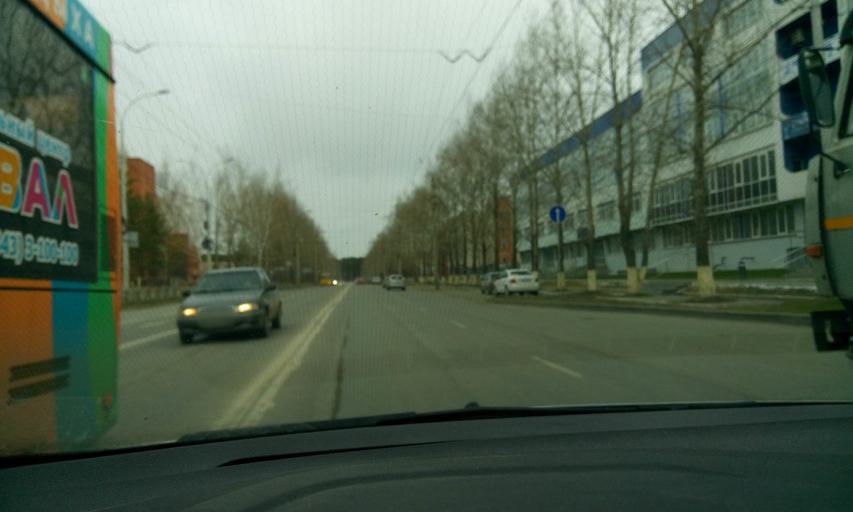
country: RU
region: Sverdlovsk
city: Sovkhoznyy
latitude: 56.7764
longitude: 60.5526
